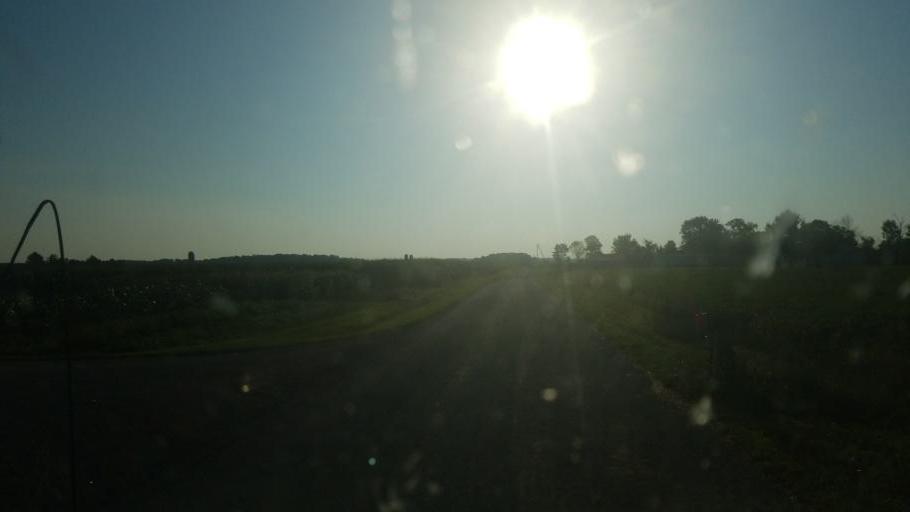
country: US
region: Ohio
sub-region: Huron County
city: Greenwich
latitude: 40.9095
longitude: -82.4668
